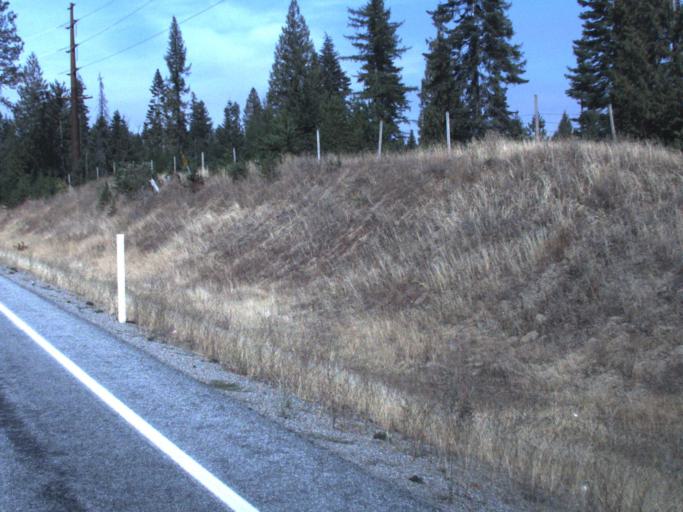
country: US
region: Washington
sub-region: Pend Oreille County
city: Newport
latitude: 48.1013
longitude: -117.2775
